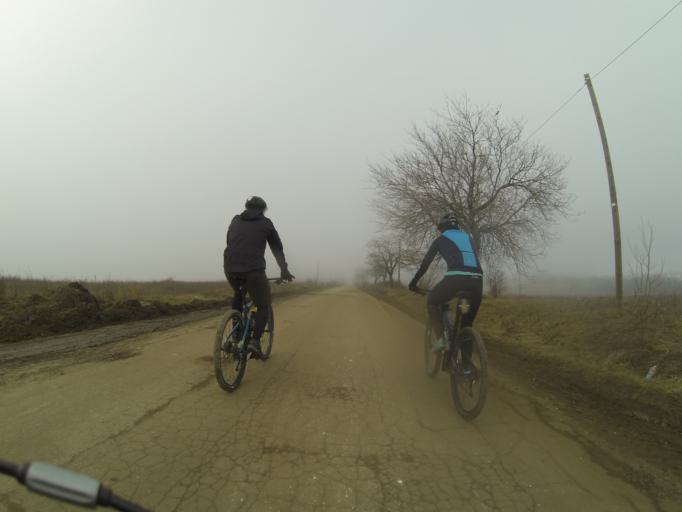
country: RO
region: Mehedinti
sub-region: Comuna Baclesu
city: Baclesu
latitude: 44.4847
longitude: 23.1022
